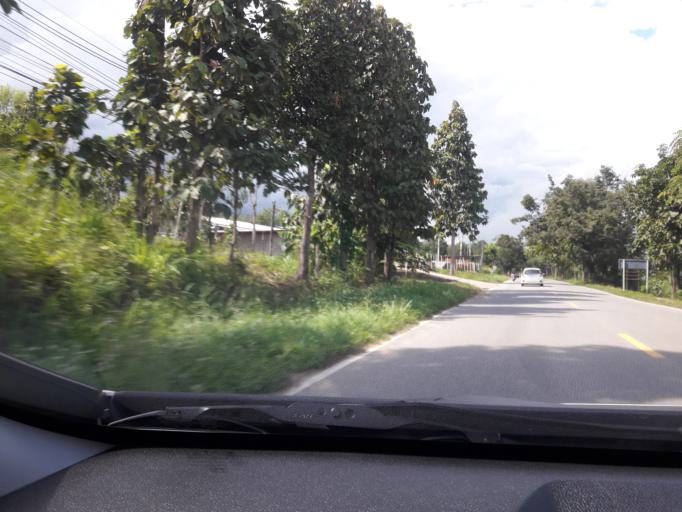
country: TH
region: Mae Hong Son
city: Mae Hi
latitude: 19.3186
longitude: 98.4386
